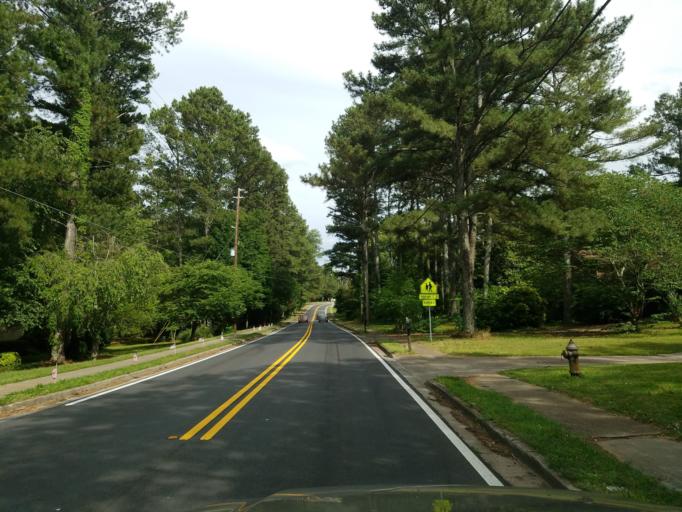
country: US
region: Georgia
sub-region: Cherokee County
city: Woodstock
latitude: 34.0282
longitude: -84.4933
